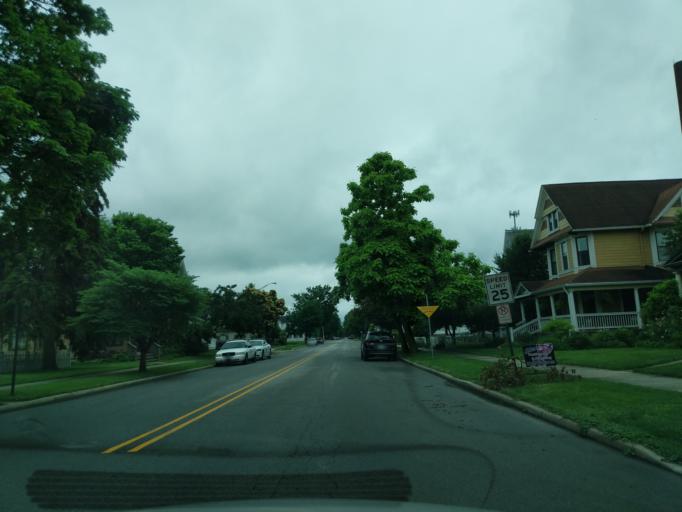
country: US
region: Indiana
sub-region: Hamilton County
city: Noblesville
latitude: 40.0429
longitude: -86.0135
